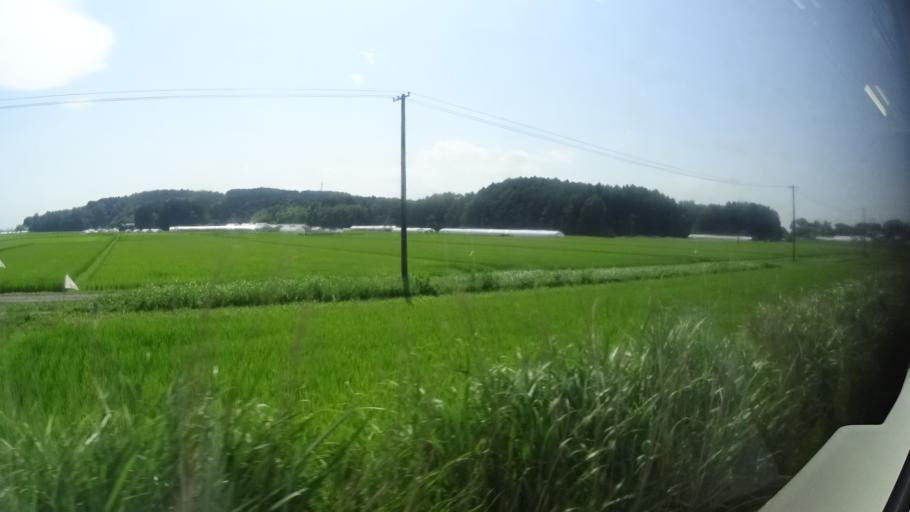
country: JP
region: Miyagi
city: Wakuya
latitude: 38.5246
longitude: 141.1599
